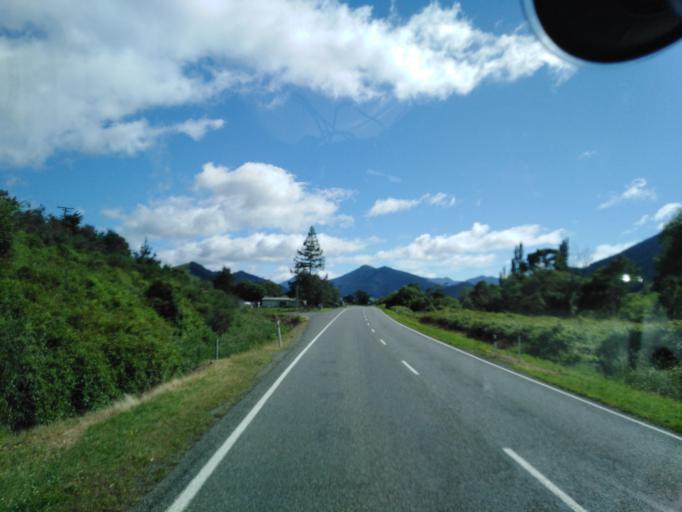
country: NZ
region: Nelson
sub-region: Nelson City
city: Nelson
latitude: -41.2450
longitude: 173.5769
